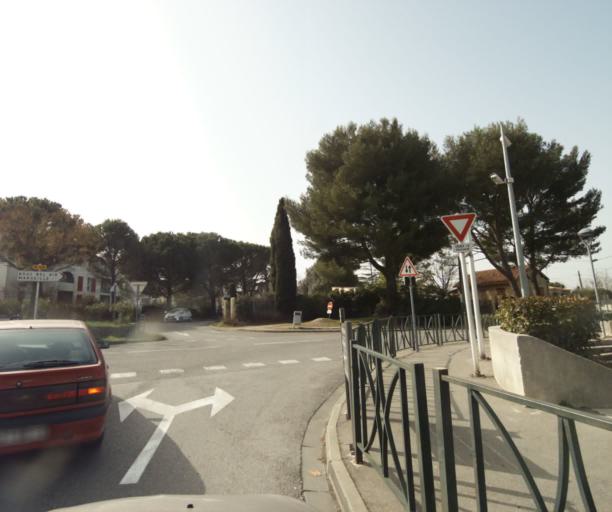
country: FR
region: Provence-Alpes-Cote d'Azur
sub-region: Departement des Bouches-du-Rhone
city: Simiane-Collongue
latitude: 43.4309
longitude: 5.4349
